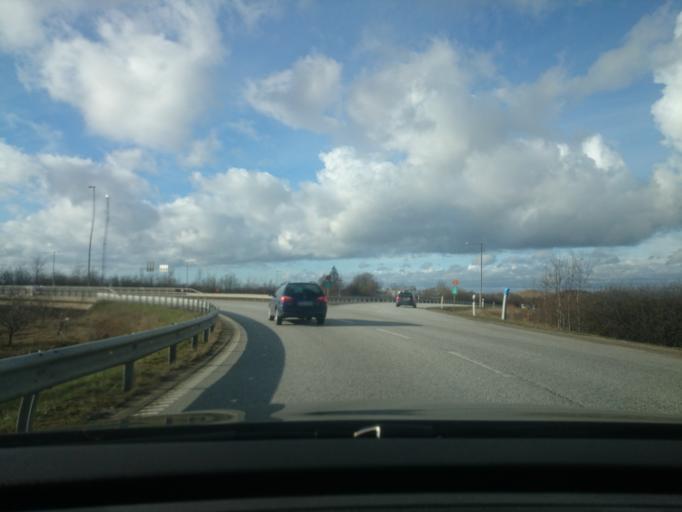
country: SE
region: Skane
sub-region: Lunds Kommun
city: Lund
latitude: 55.7191
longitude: 13.2251
